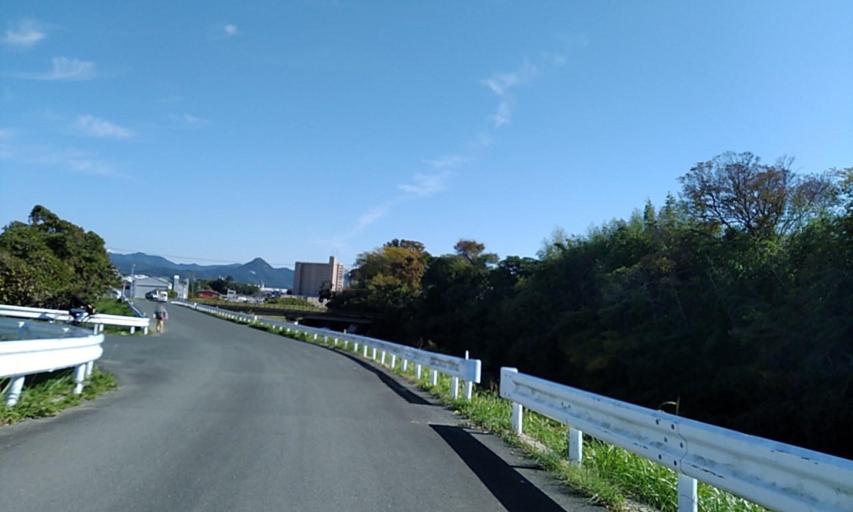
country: JP
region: Aichi
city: Toyohashi
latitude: 34.7721
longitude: 137.3993
